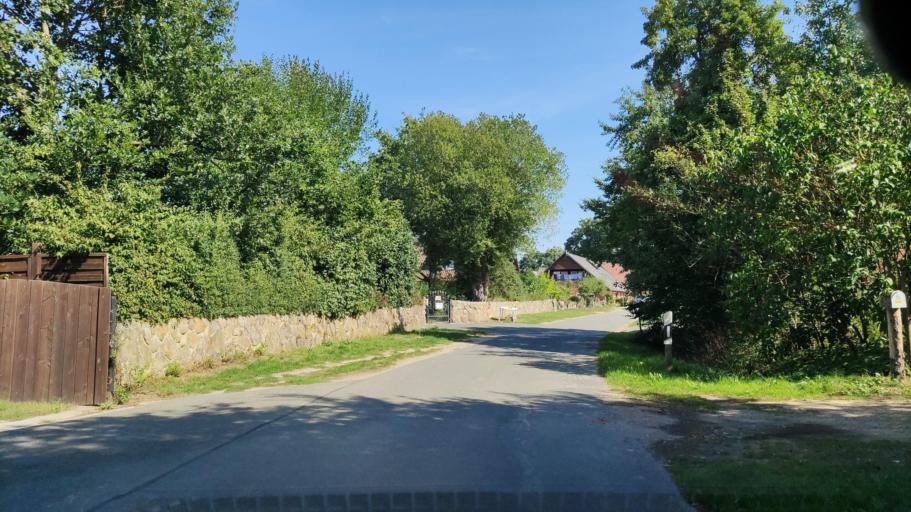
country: DE
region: Lower Saxony
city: Hitzacker
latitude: 53.1473
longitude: 10.9820
